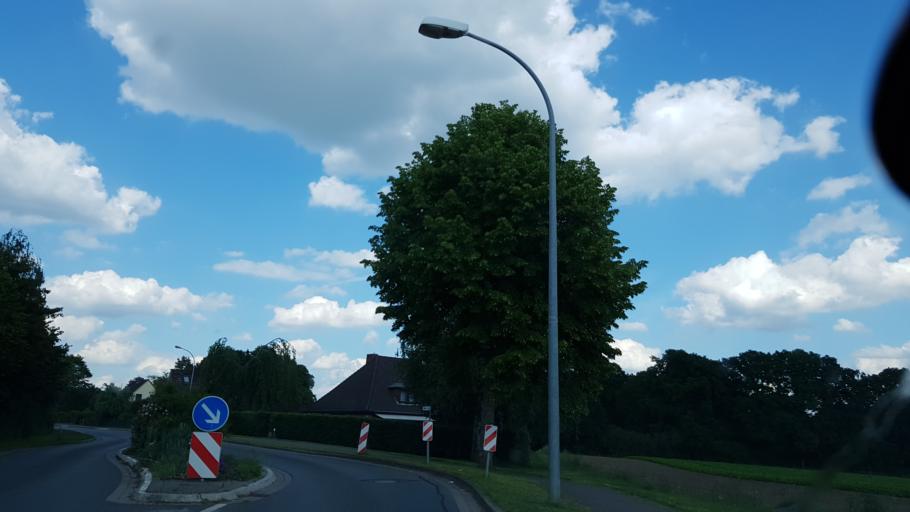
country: DE
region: Lower Saxony
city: Wenzendorf
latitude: 53.3494
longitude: 9.7655
